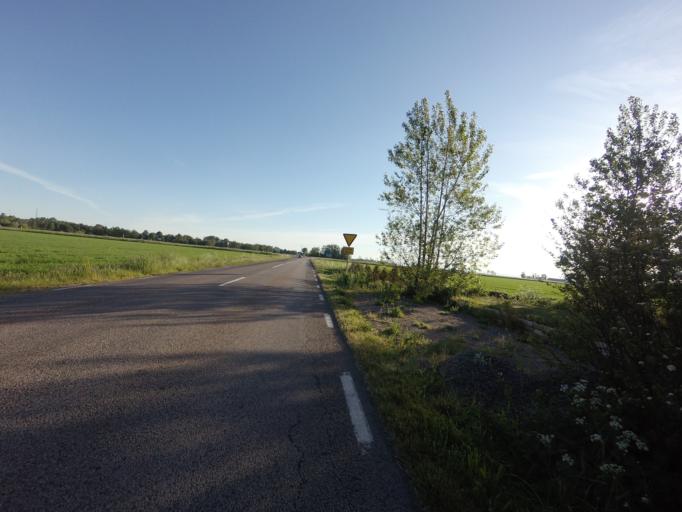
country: SE
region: Skane
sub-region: Hoganas Kommun
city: Hoganas
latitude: 56.2139
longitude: 12.6783
